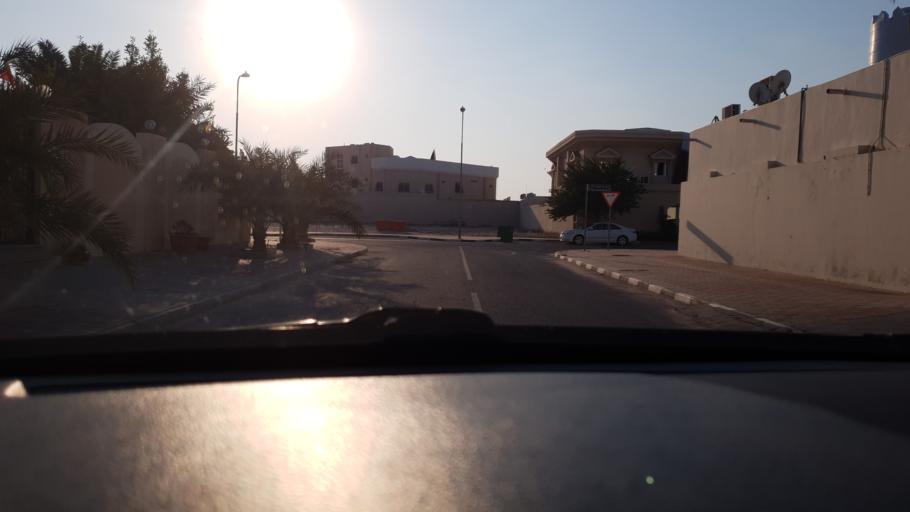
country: QA
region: Baladiyat ad Dawhah
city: Doha
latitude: 25.2360
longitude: 51.5626
